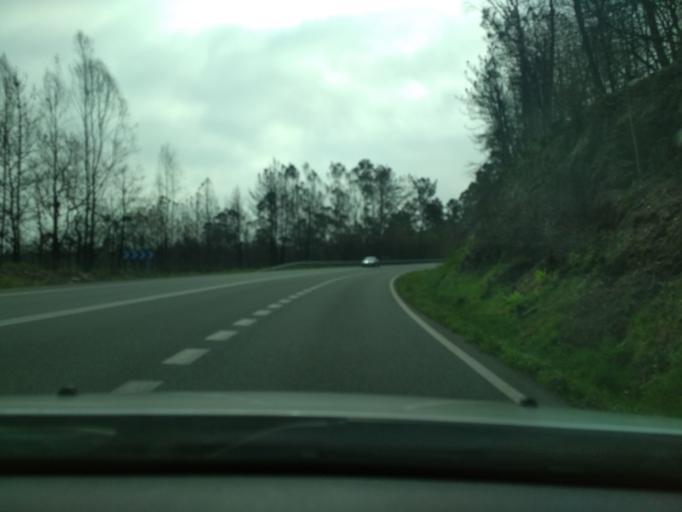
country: ES
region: Galicia
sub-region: Provincia de Pontevedra
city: Catoira
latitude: 42.6532
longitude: -8.6818
